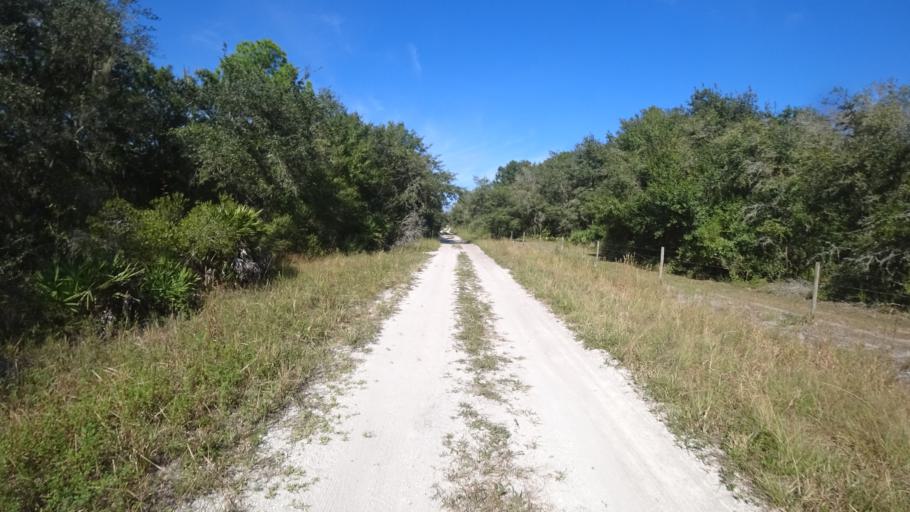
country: US
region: Florida
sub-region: DeSoto County
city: Arcadia
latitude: 27.2908
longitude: -82.0643
